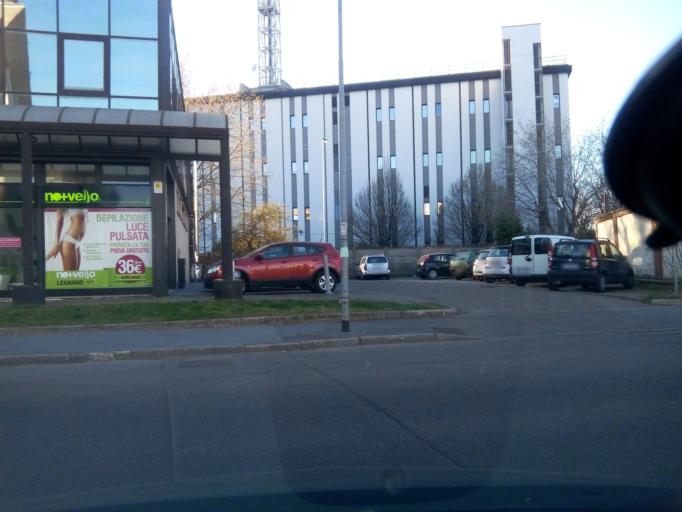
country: IT
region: Lombardy
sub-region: Citta metropolitana di Milano
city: Legnano
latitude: 45.5997
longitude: 8.9158
